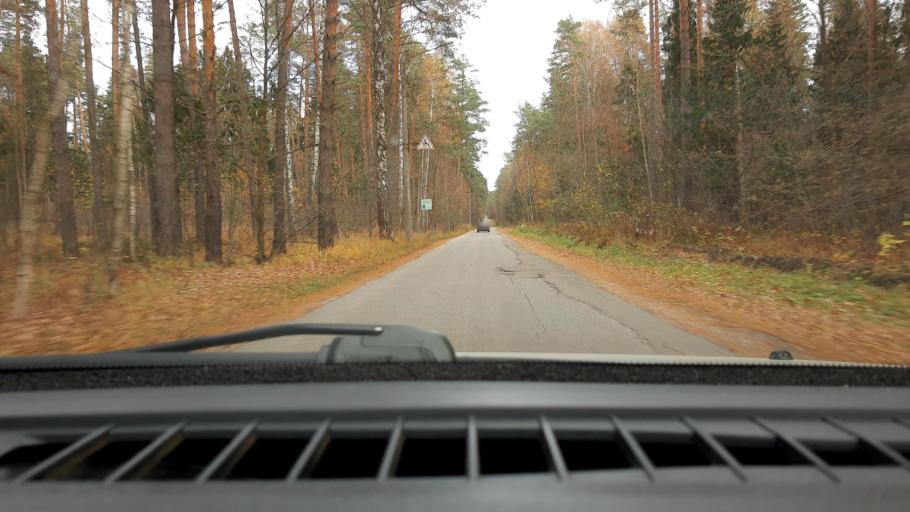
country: RU
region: Nizjnij Novgorod
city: Afonino
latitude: 56.1690
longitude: 44.0984
